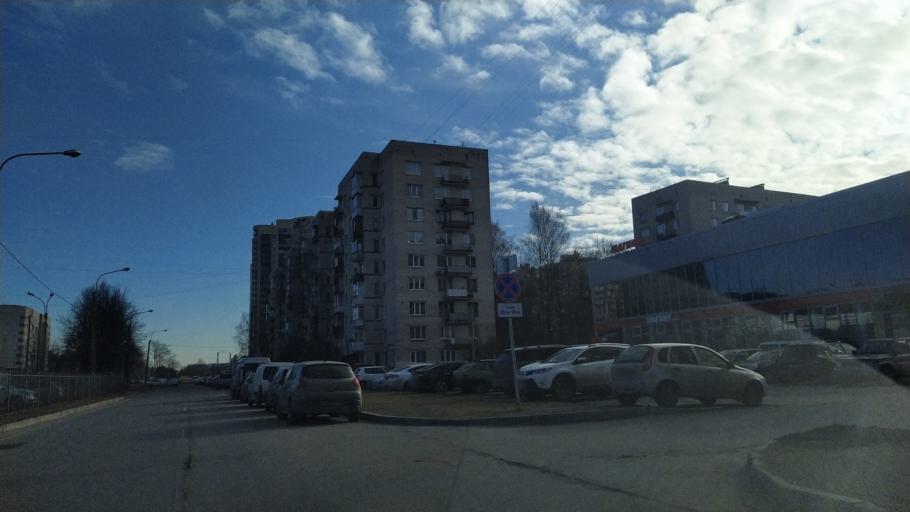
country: RU
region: Leningrad
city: Akademicheskoe
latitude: 60.0082
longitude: 30.3985
